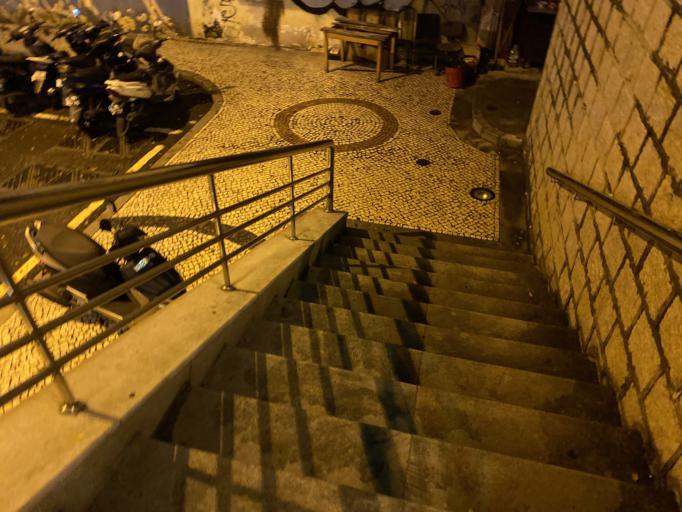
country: MO
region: Macau
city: Macau
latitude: 22.1969
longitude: 113.5475
